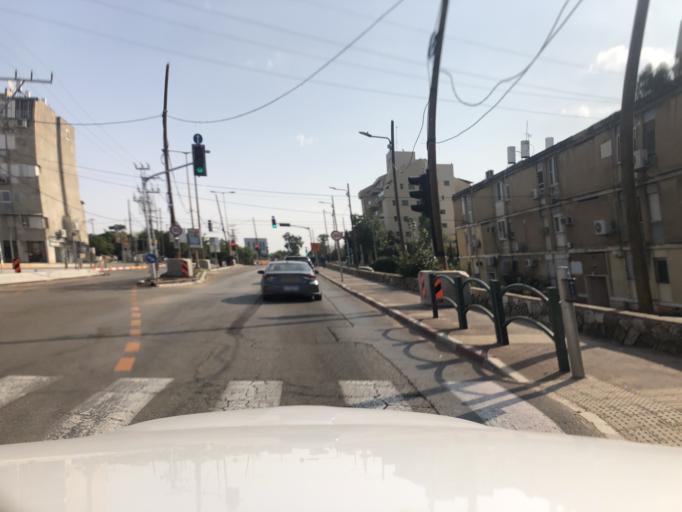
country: IL
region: Central District
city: Kfar Saba
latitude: 32.1724
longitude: 34.9208
